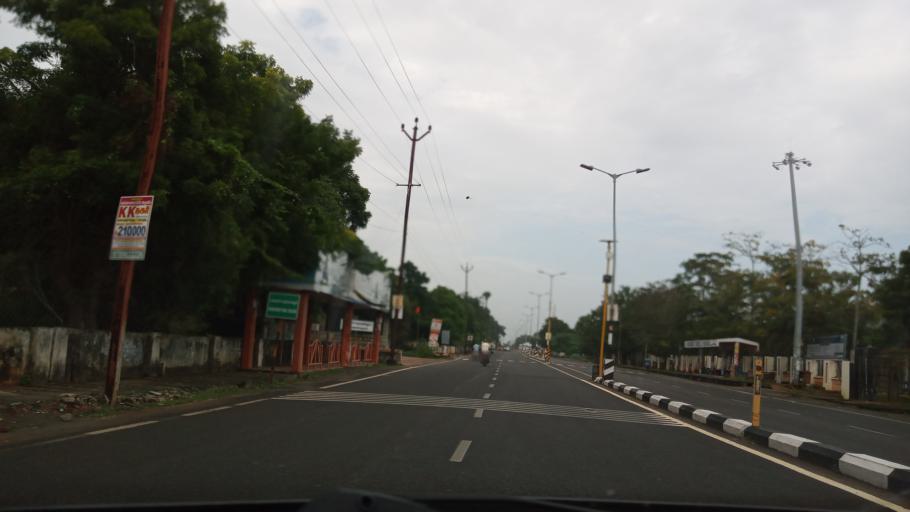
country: IN
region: Tamil Nadu
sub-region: Villupuram
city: Auroville
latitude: 12.0119
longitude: 79.8572
